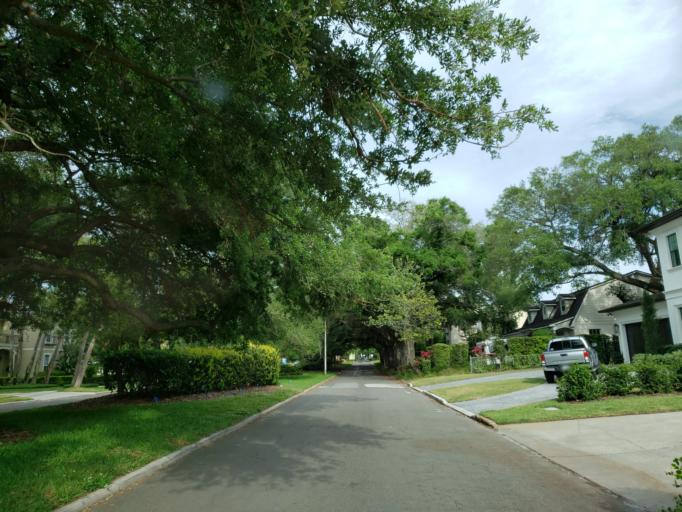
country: US
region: Florida
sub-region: Hillsborough County
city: Tampa
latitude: 27.9376
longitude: -82.5169
